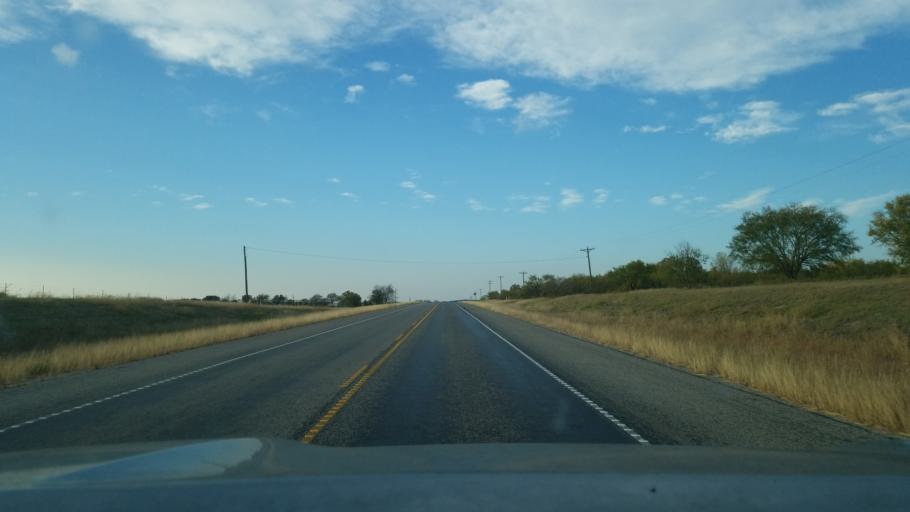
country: US
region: Texas
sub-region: Brown County
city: Lake Brownwood
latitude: 32.0297
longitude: -98.9319
